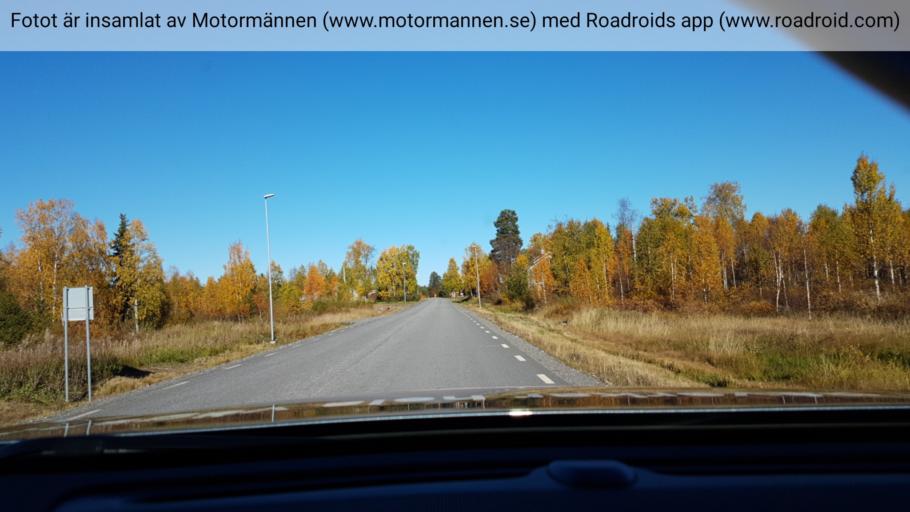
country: SE
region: Norrbotten
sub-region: Gallivare Kommun
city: Gaellivare
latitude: 66.7519
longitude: 20.9472
